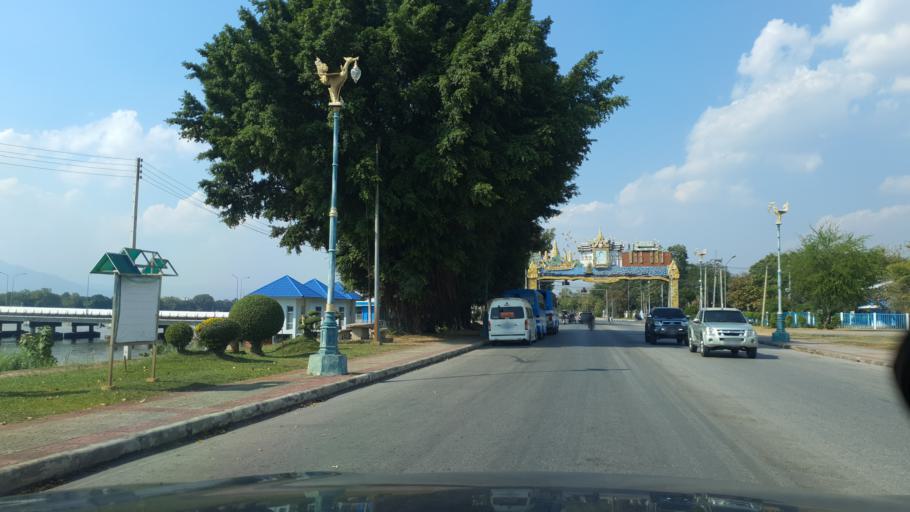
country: TH
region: Tak
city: Tak
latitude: 16.8828
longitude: 99.1183
